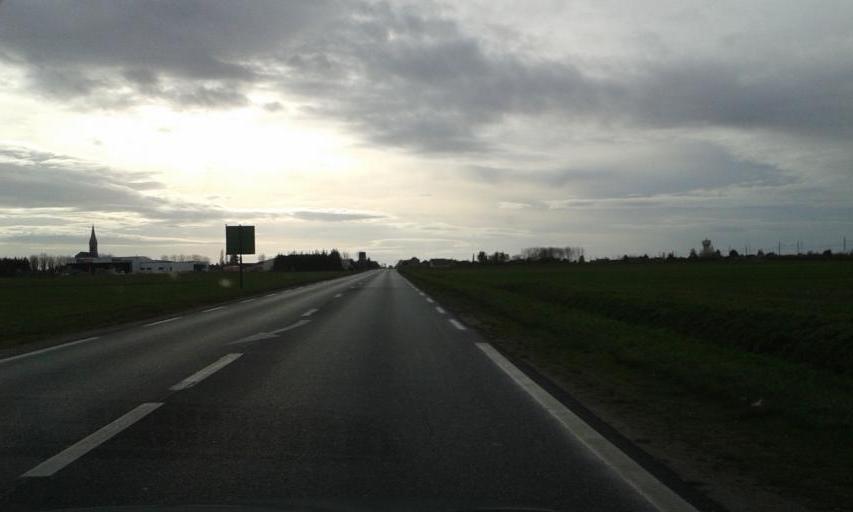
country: FR
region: Centre
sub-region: Departement du Loiret
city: Baule
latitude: 47.8168
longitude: 1.6783
